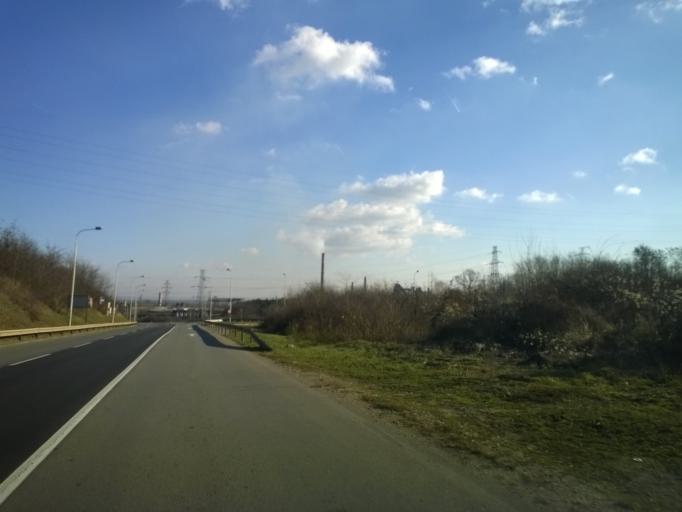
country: RS
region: Central Serbia
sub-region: Podunavski Okrug
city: Smederevo
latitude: 44.6096
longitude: 20.9550
